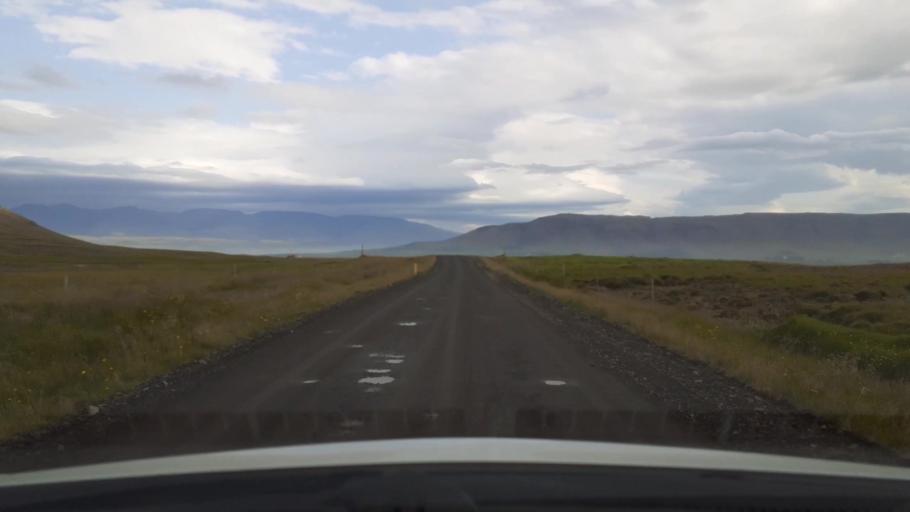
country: IS
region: Capital Region
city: Mosfellsbaer
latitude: 64.3068
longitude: -21.6564
